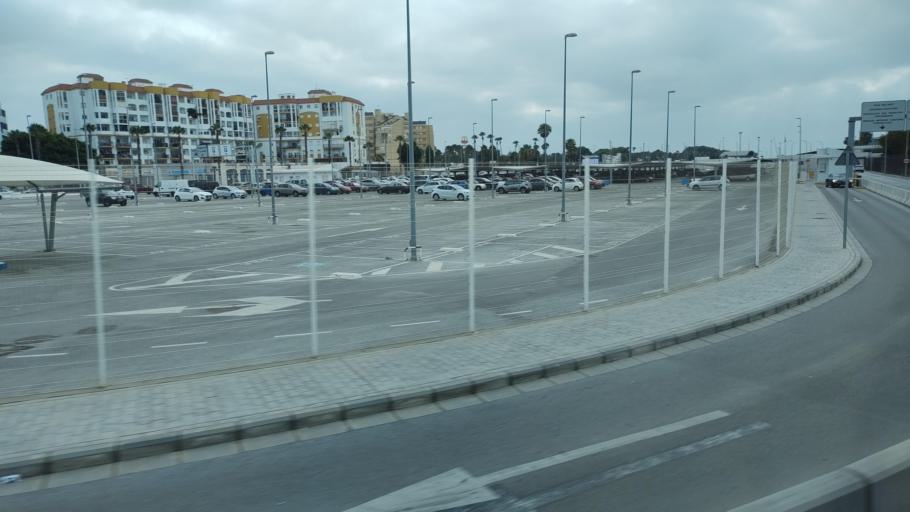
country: GI
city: Gibraltar
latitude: 36.1551
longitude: -5.3518
